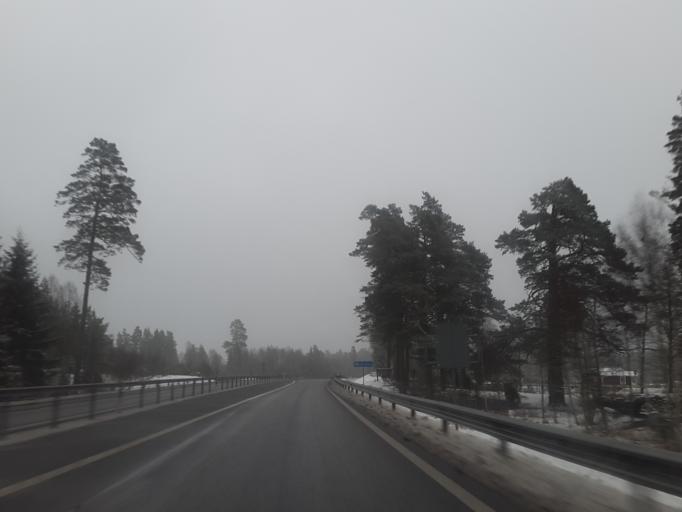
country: SE
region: Joenkoeping
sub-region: Mullsjo Kommun
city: Mullsjoe
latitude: 57.7691
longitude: 13.7968
